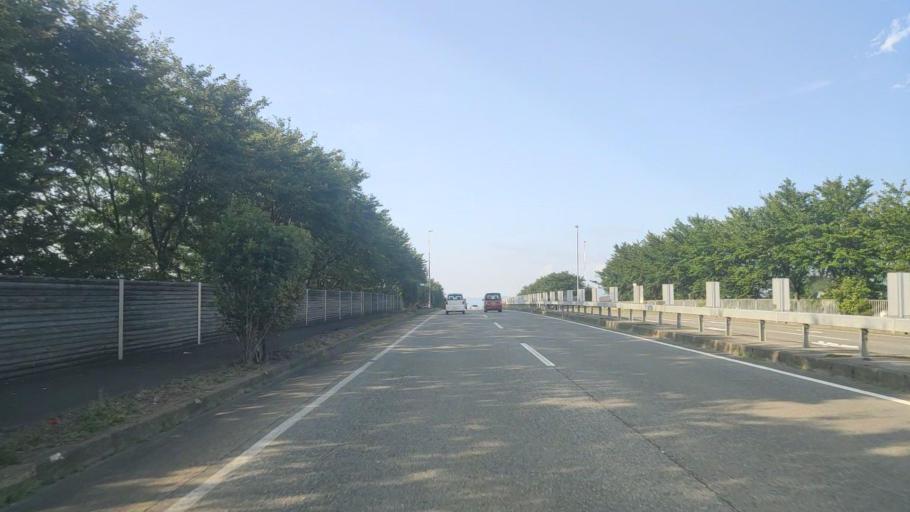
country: JP
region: Fukui
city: Fukui-shi
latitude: 36.0337
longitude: 136.2271
